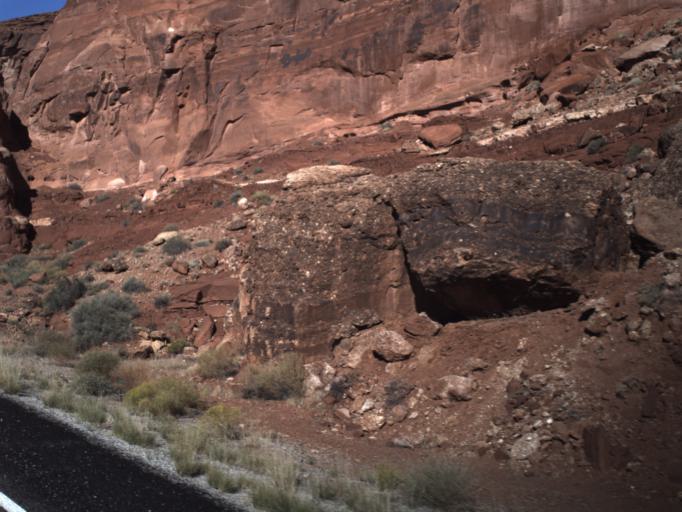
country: US
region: Utah
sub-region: San Juan County
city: Blanding
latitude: 37.8897
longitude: -110.4049
